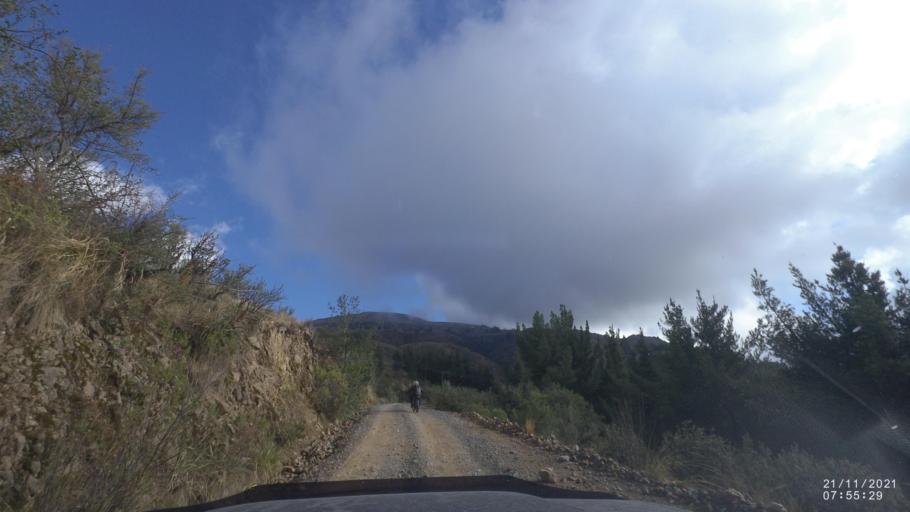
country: BO
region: Cochabamba
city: Cochabamba
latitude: -17.3002
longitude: -66.2181
